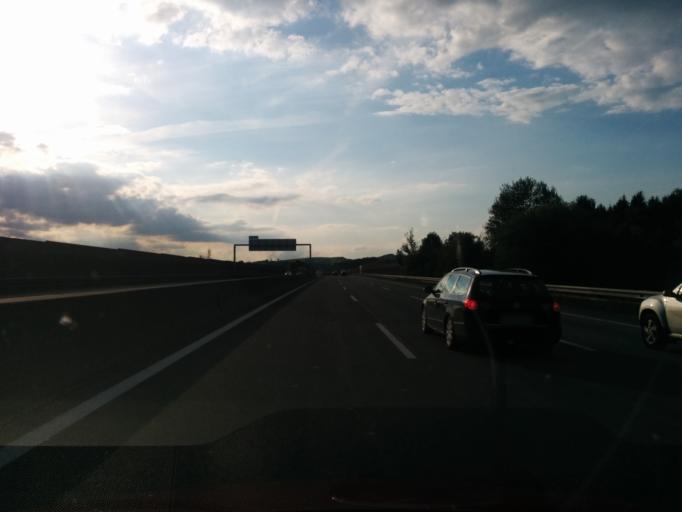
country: AT
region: Lower Austria
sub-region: Politischer Bezirk Melk
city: Blindenmarkt
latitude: 48.1305
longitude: 15.0009
